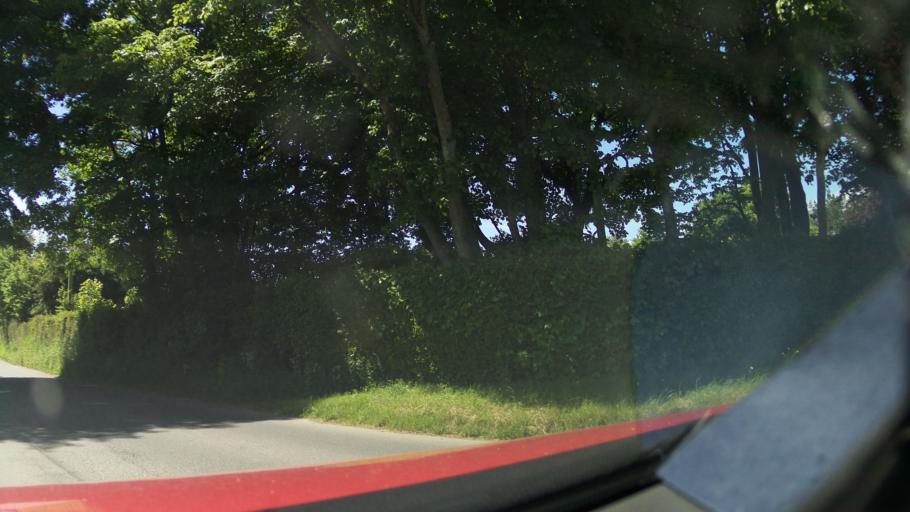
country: GB
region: England
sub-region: Devon
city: Ottery St Mary
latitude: 50.7595
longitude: -3.2737
